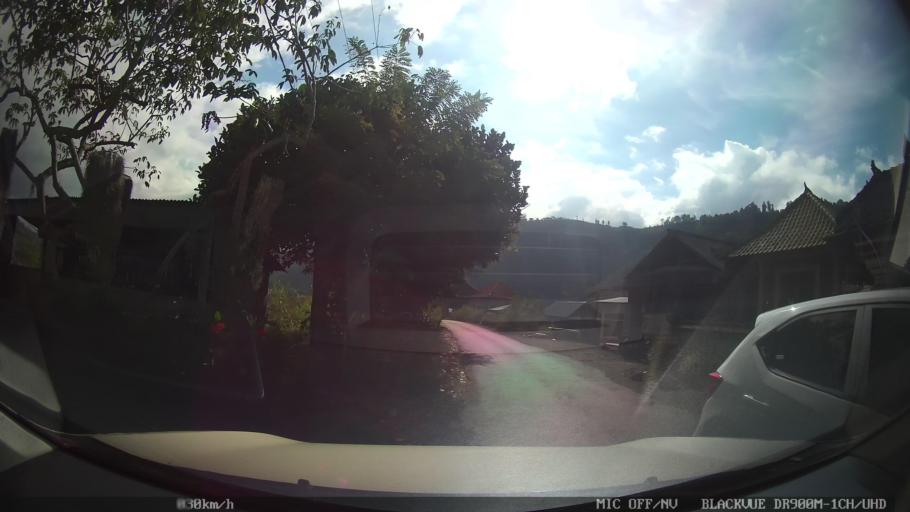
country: ID
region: Bali
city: Banjar Trunyan
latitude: -8.2147
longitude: 115.3731
